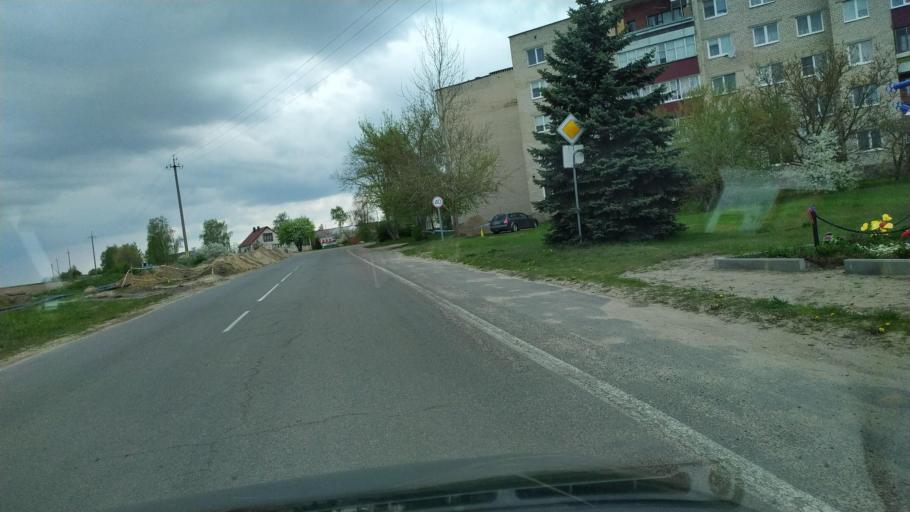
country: BY
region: Brest
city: Pruzhany
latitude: 52.5647
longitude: 24.4211
